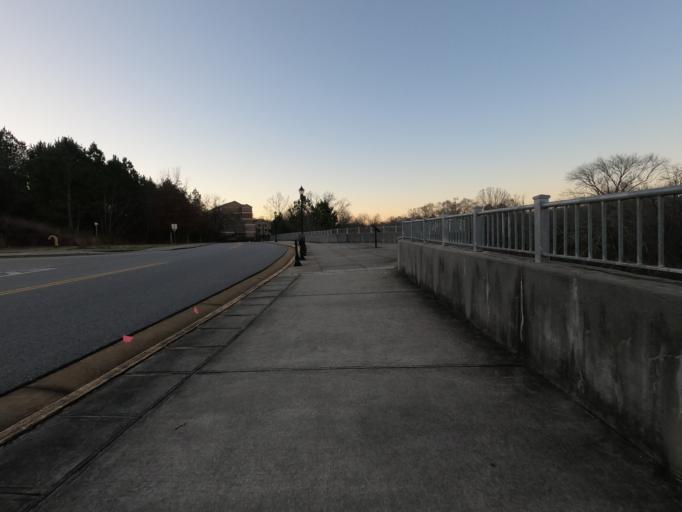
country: US
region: Georgia
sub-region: Clarke County
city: Athens
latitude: 33.9624
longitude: -83.3702
